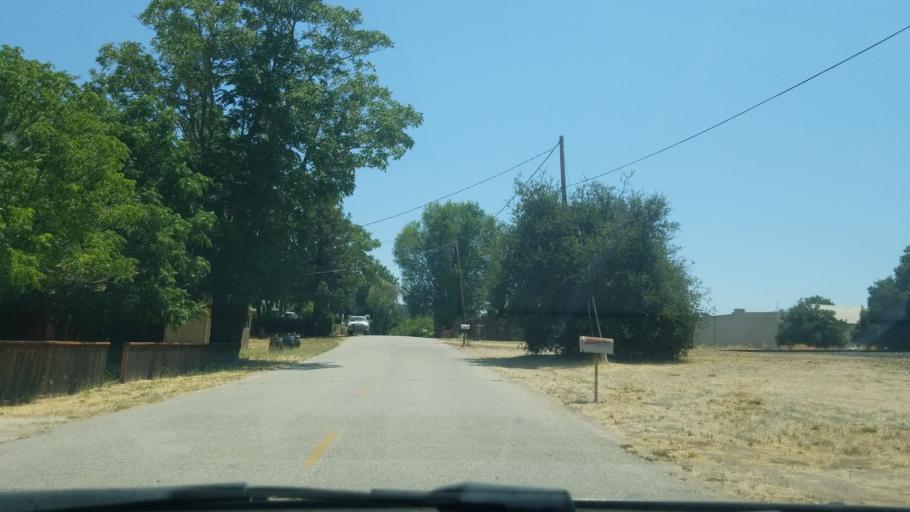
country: US
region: California
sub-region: San Luis Obispo County
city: Atascadero
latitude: 35.5077
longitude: -120.6672
